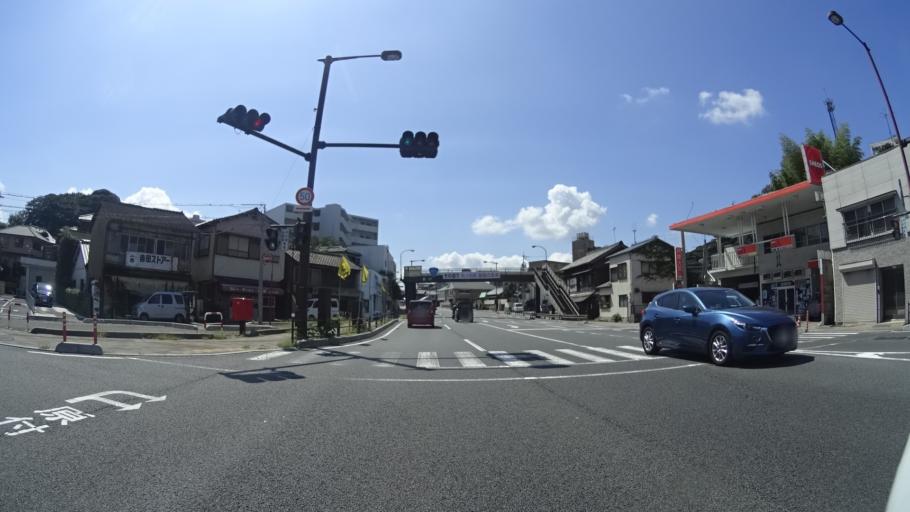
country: JP
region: Yamaguchi
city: Shimonoseki
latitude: 33.9657
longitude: 130.9186
